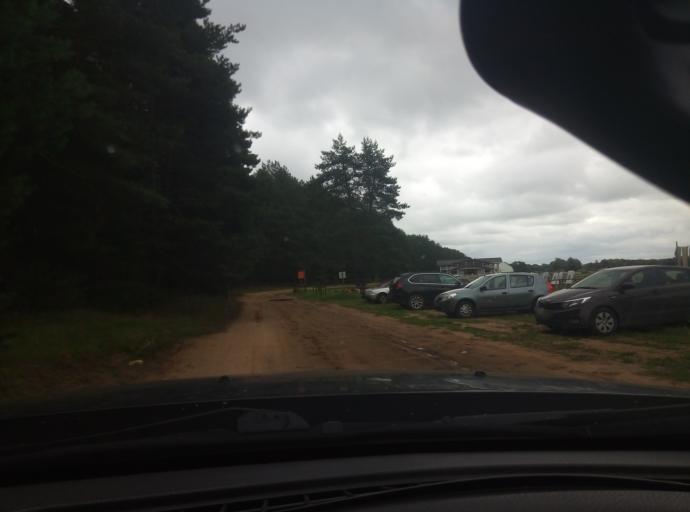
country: RU
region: Kaluga
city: Zhukovo
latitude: 54.9551
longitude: 36.7667
